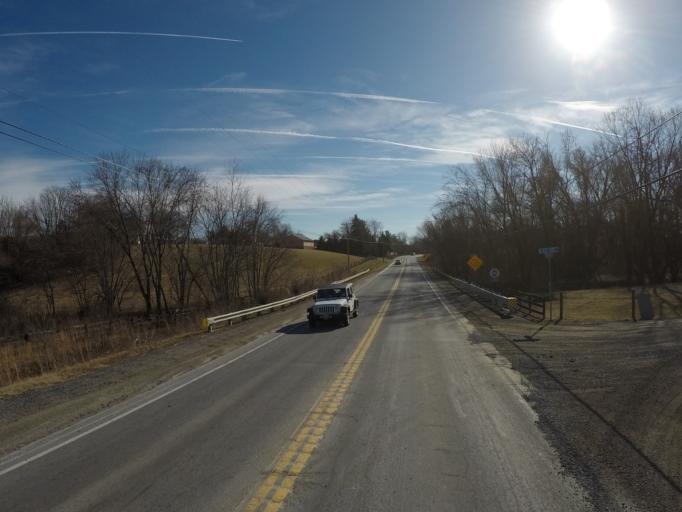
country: US
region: Maryland
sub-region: Frederick County
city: Point of Rocks
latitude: 39.2217
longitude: -77.5341
